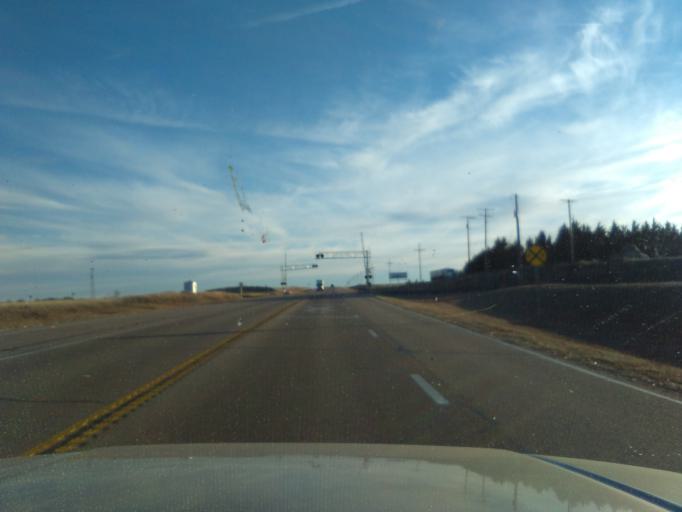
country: US
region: Kansas
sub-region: Logan County
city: Oakley
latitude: 39.1449
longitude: -100.8680
